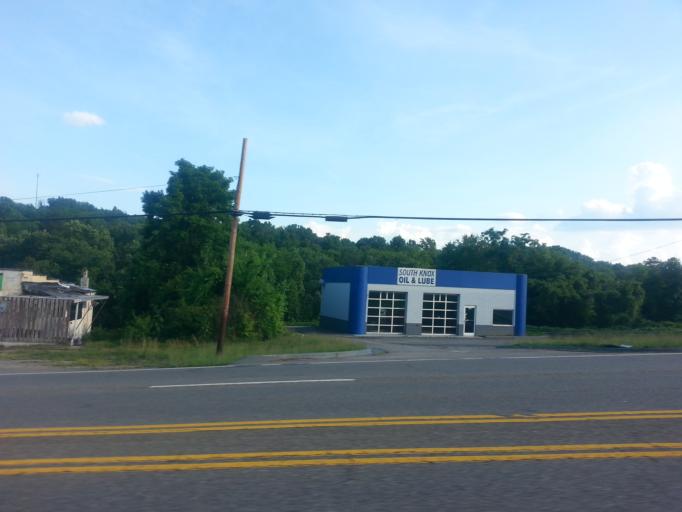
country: US
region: Tennessee
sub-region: Knox County
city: Knoxville
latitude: 35.9212
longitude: -83.8635
